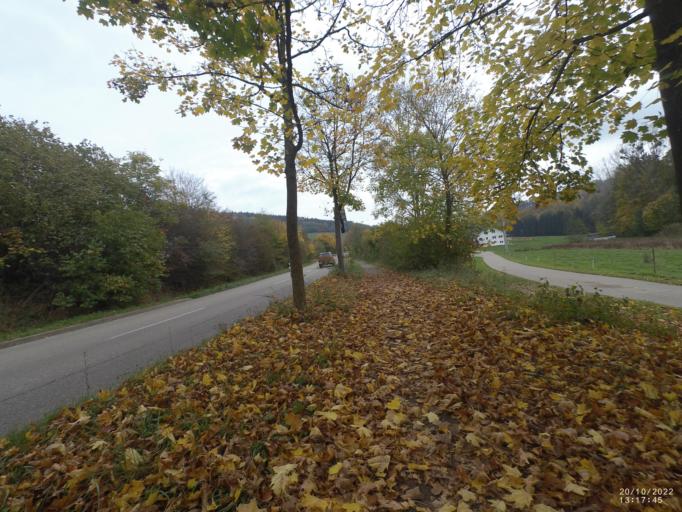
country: DE
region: Baden-Wuerttemberg
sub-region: Regierungsbezirk Stuttgart
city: Donzdorf
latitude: 48.7094
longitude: 9.8017
